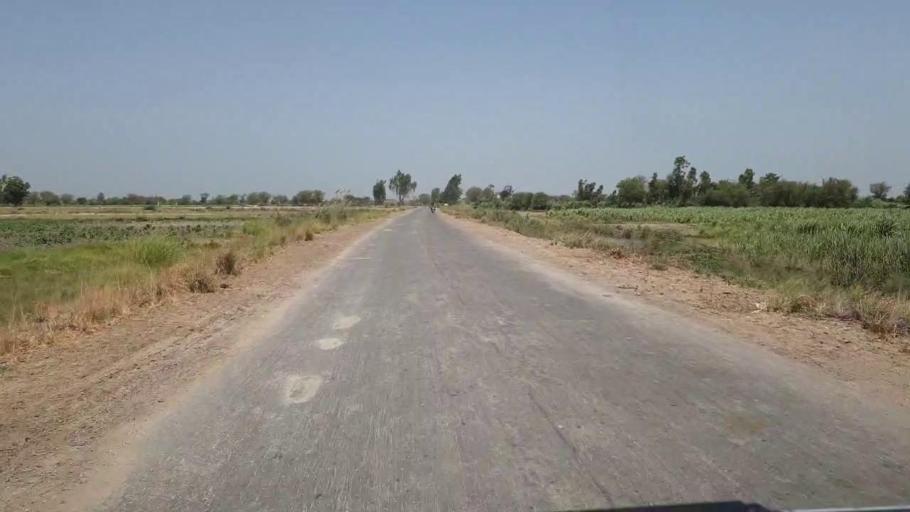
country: PK
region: Sindh
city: Nawabshah
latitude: 26.3426
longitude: 68.3735
